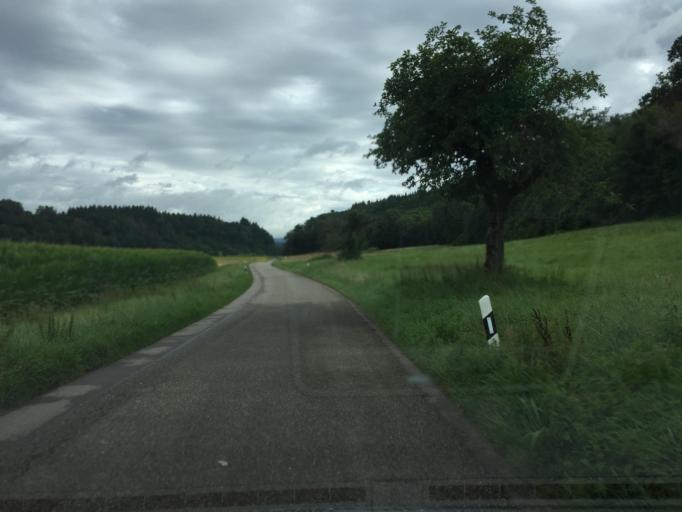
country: CH
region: Schaffhausen
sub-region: Bezirk Unterklettgau
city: Wilchingen
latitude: 47.6350
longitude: 8.4463
